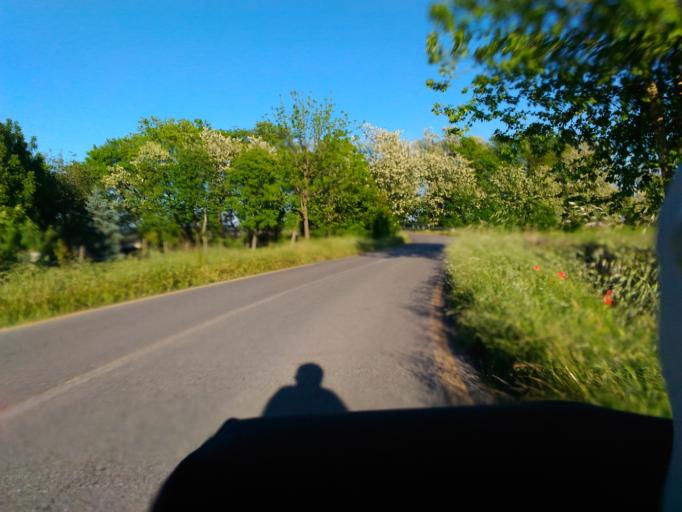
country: IT
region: Lombardy
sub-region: Provincia di Lodi
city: Lodi Vecchio
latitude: 45.3007
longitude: 9.4047
